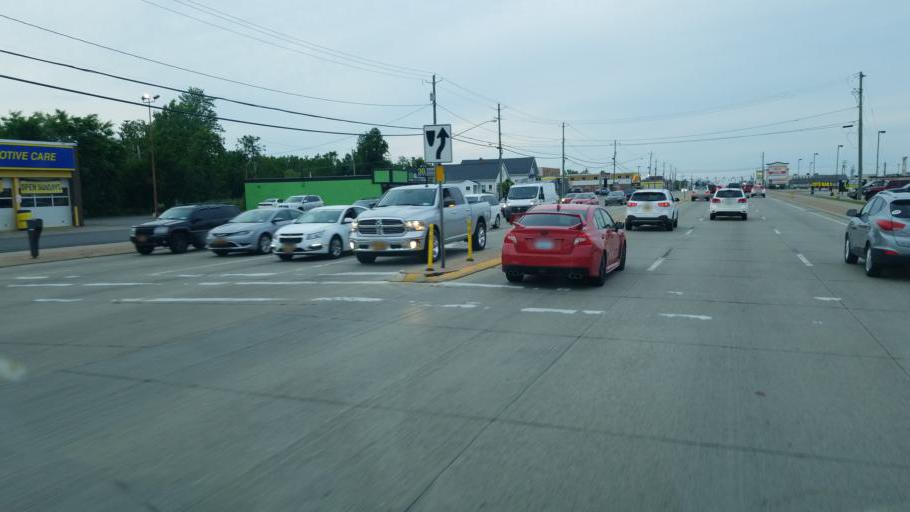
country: US
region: New York
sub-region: Erie County
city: Harris Hill
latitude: 42.9614
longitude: -78.6968
